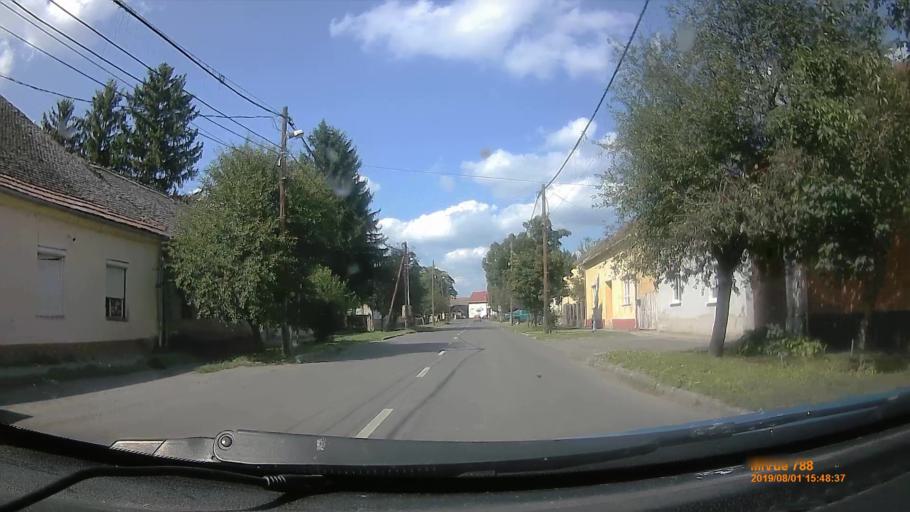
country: HU
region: Baranya
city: Szentlorinc
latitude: 46.0386
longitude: 17.9857
